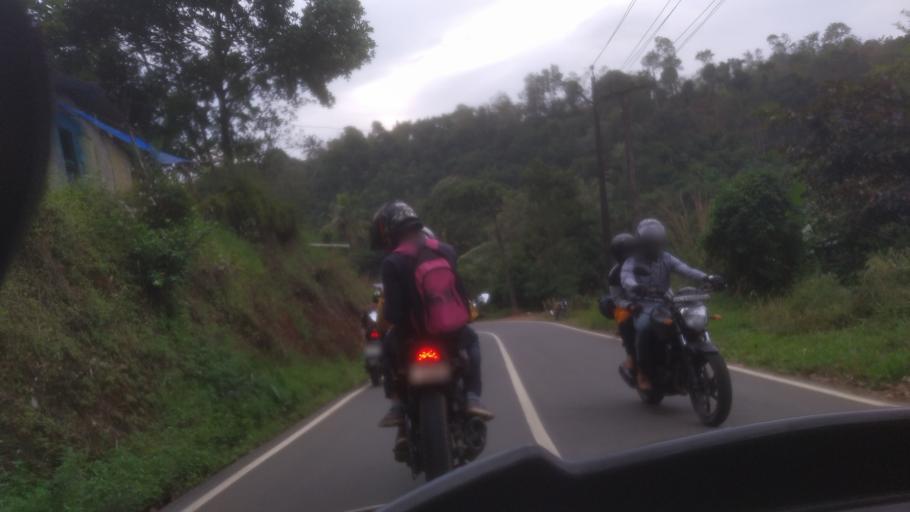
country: IN
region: Kerala
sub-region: Idukki
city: Idukki
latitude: 9.9477
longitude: 77.0135
